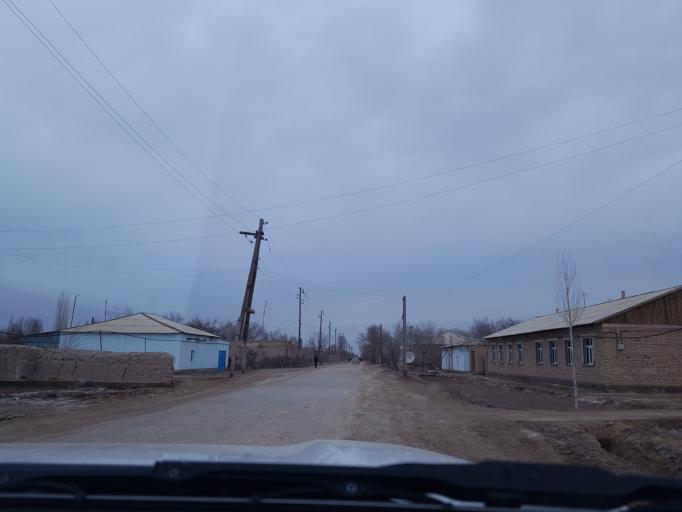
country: TM
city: Akdepe
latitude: 41.9824
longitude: 59.4756
